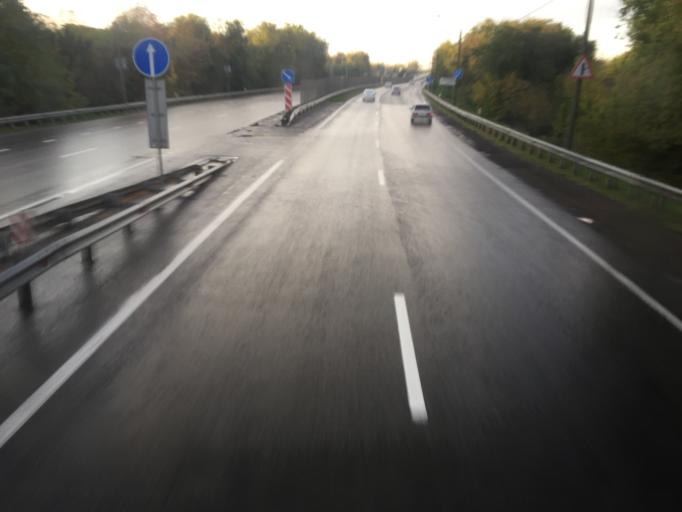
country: RU
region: Rostov
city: Bataysk
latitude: 47.1288
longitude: 39.7747
